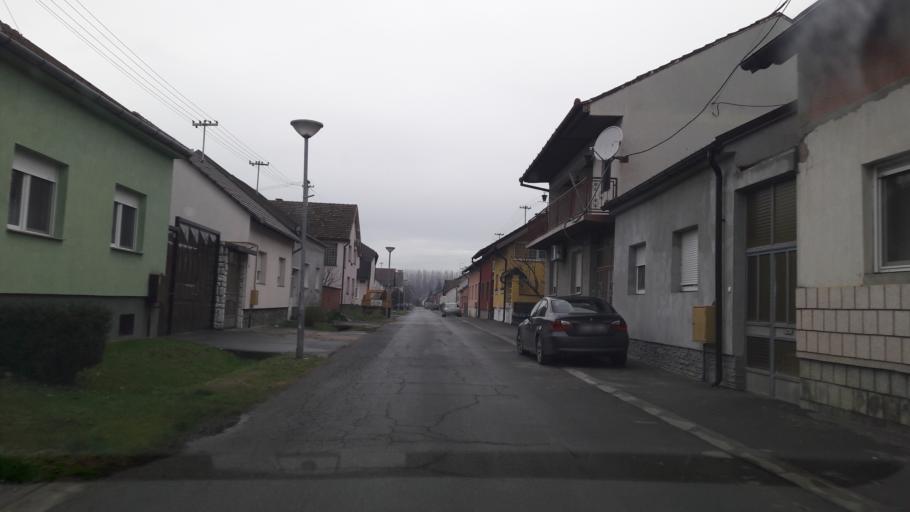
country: HR
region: Osjecko-Baranjska
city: Visnjevac
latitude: 45.5698
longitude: 18.6191
